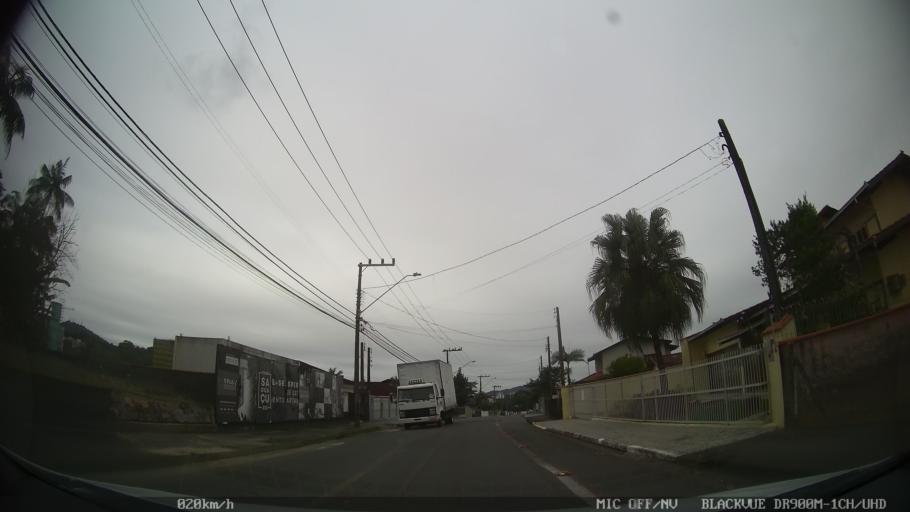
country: BR
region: Santa Catarina
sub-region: Joinville
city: Joinville
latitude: -26.2709
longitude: -48.8398
